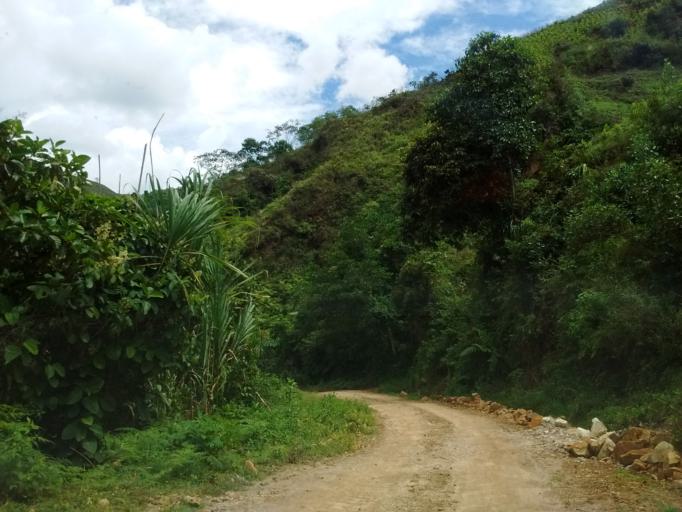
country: CO
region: Cauca
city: Morales
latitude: 2.6813
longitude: -76.7641
